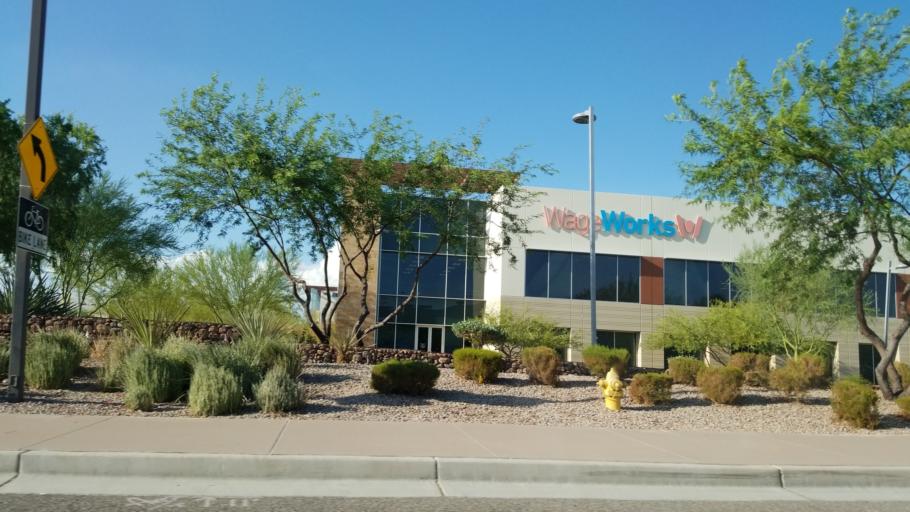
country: US
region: Arizona
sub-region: Maricopa County
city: Tempe Junction
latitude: 33.4314
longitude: -111.9663
